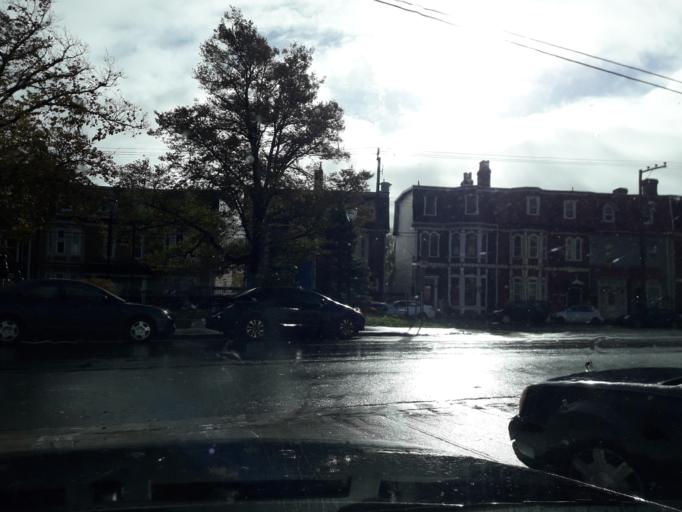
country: CA
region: Newfoundland and Labrador
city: St. John's
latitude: 47.5648
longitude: -52.7101
